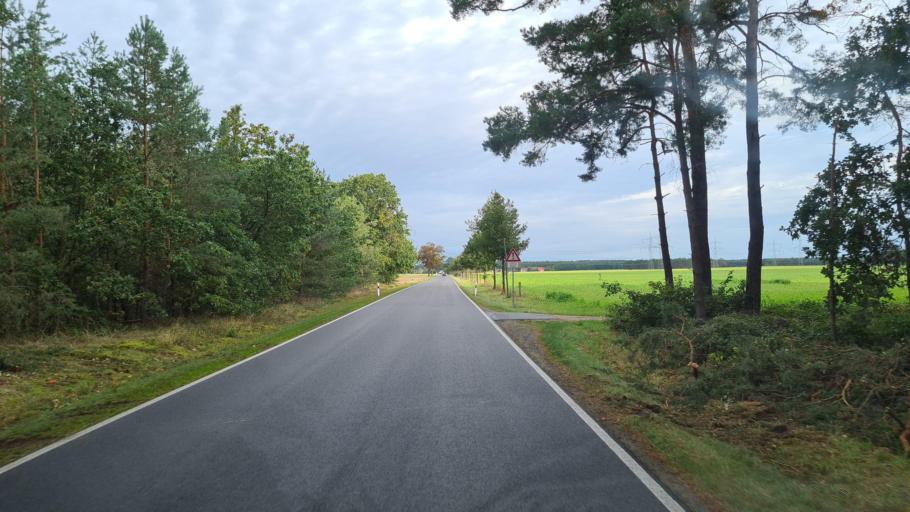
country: DE
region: Brandenburg
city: Luckau
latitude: 51.8901
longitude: 13.7153
